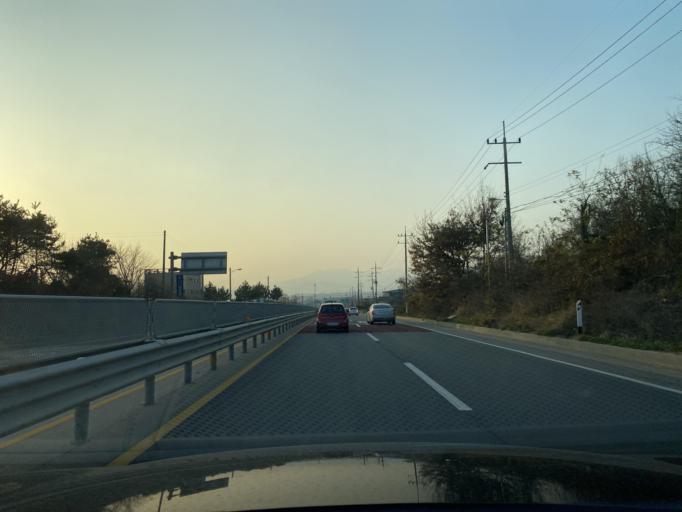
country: KR
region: Chungcheongnam-do
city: Yesan
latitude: 36.6903
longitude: 126.7472
